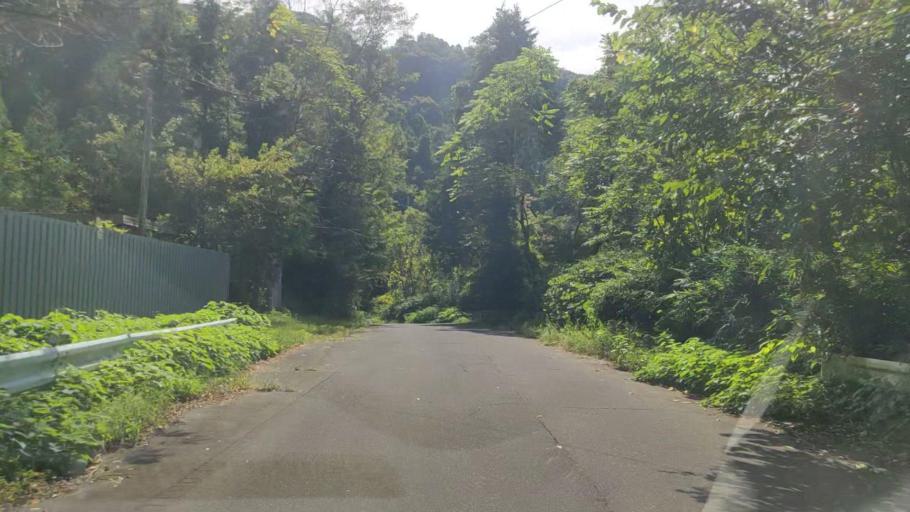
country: JP
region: Gunma
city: Numata
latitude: 36.5871
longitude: 139.0584
